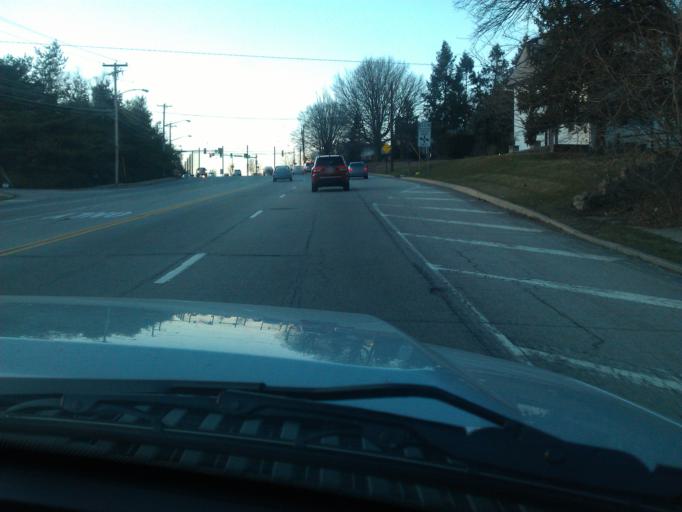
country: US
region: Pennsylvania
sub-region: Montgomery County
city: Plymouth Meeting
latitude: 40.1203
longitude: -75.2873
